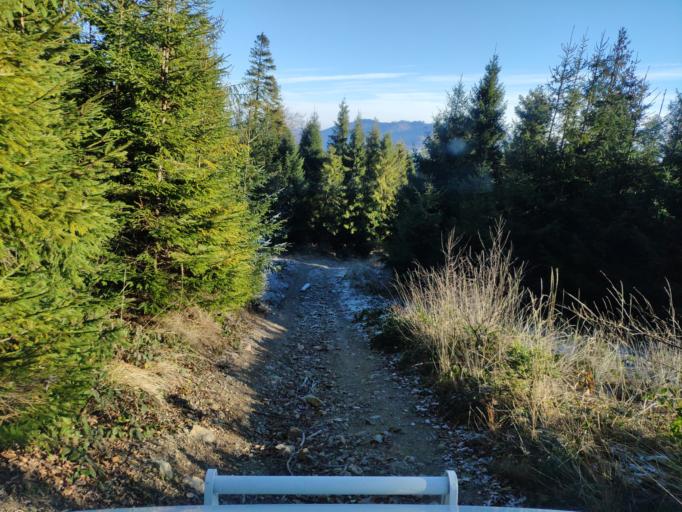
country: SK
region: Kosicky
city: Dobsina
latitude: 48.8164
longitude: 20.4740
